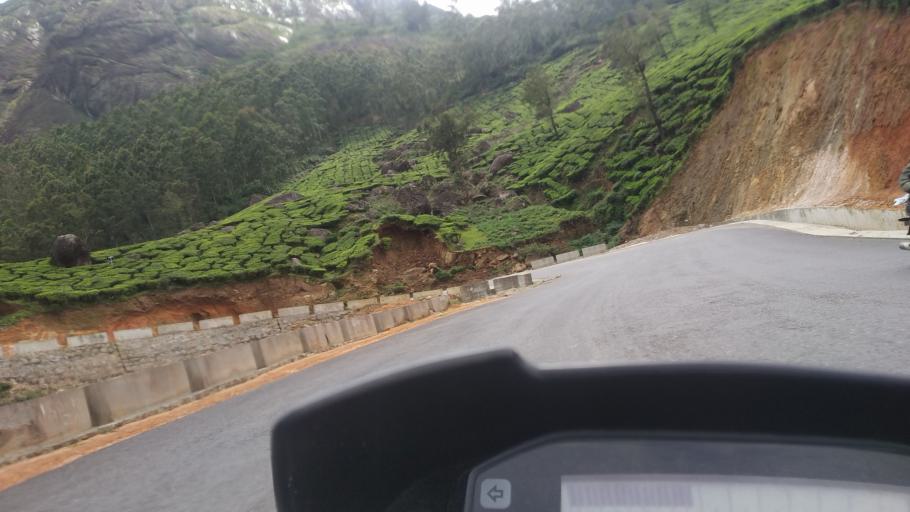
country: IN
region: Kerala
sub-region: Idukki
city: Munnar
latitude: 10.0436
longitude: 77.1111
